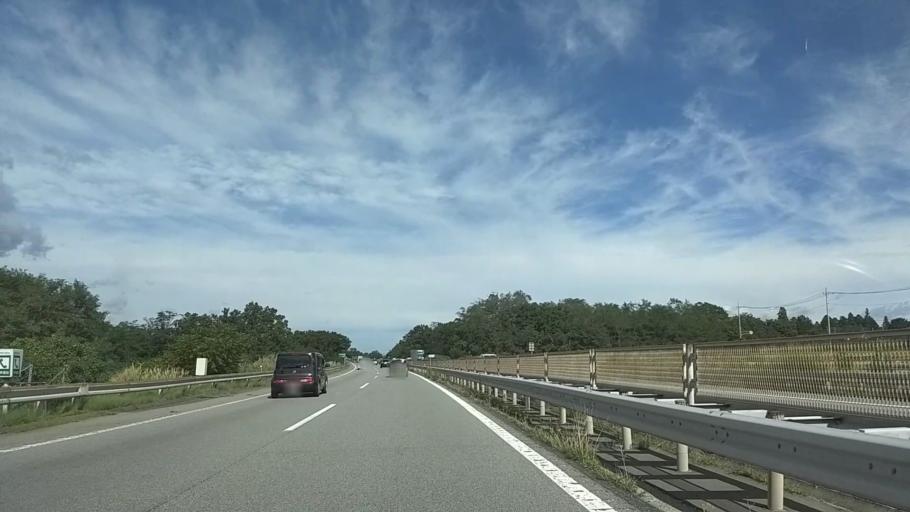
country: JP
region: Yamanashi
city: Nirasaki
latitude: 35.7408
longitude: 138.4496
